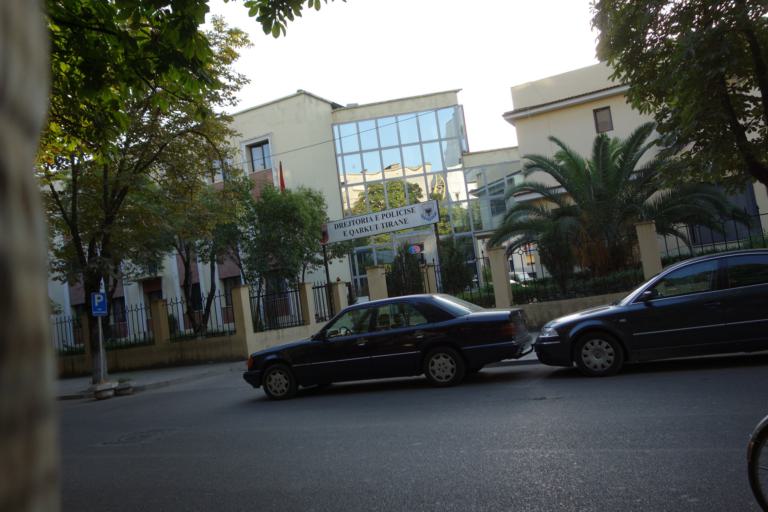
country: AL
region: Tirane
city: Tirana
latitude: 41.3241
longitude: 19.8130
